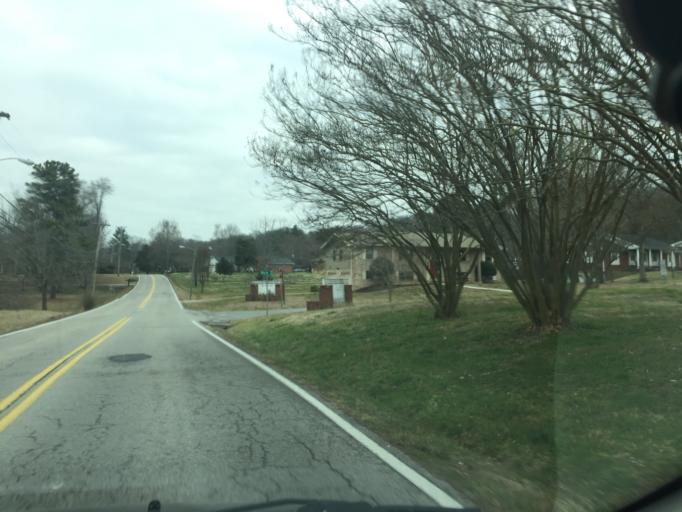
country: US
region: Tennessee
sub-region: Hamilton County
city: East Brainerd
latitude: 35.0087
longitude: -85.1286
